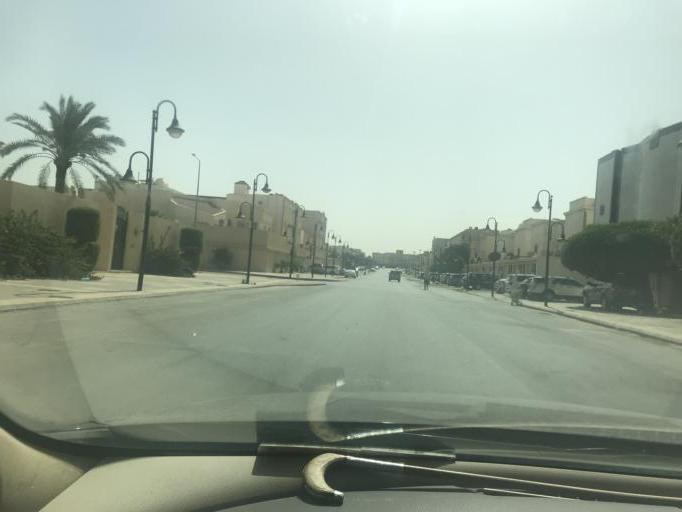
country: SA
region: Ar Riyad
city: Riyadh
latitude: 24.7712
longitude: 46.7096
